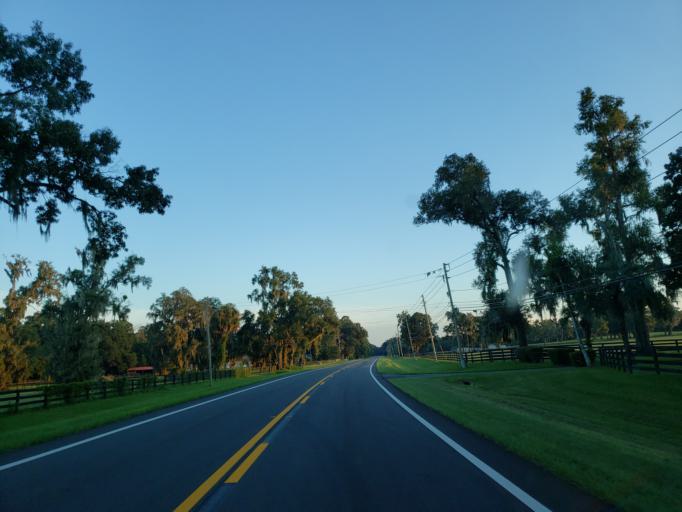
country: US
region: Florida
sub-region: Marion County
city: Citra
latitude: 29.3954
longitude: -82.2060
